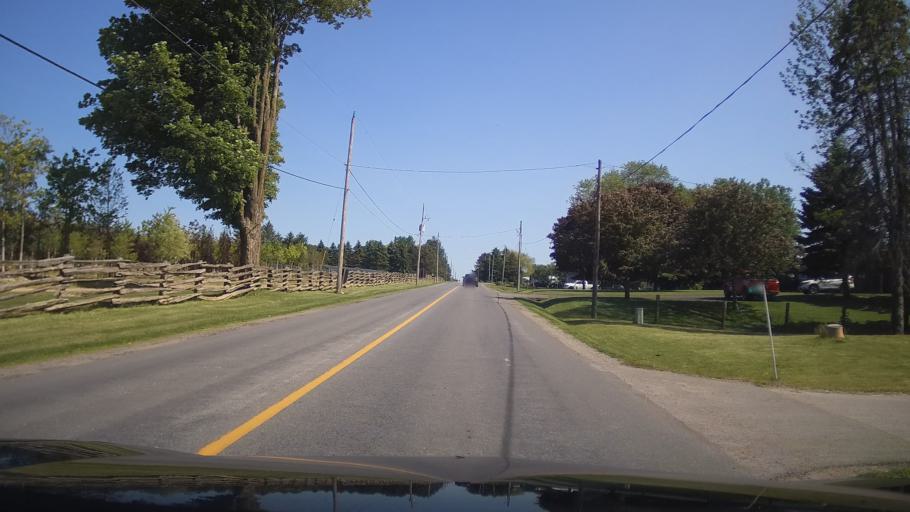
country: CA
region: Ontario
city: Oshawa
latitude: 43.9654
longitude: -78.7357
